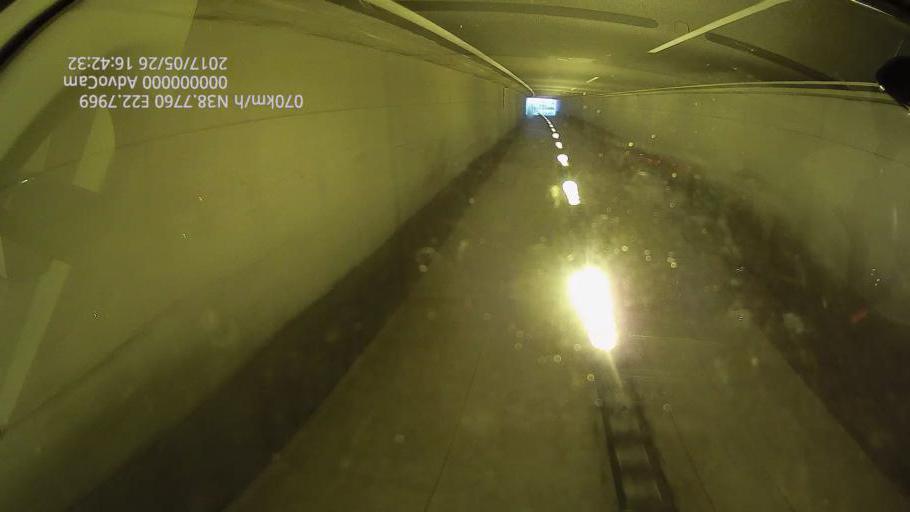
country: GR
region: Central Greece
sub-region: Nomos Fthiotidos
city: Stylida
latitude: 38.9029
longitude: 22.5630
